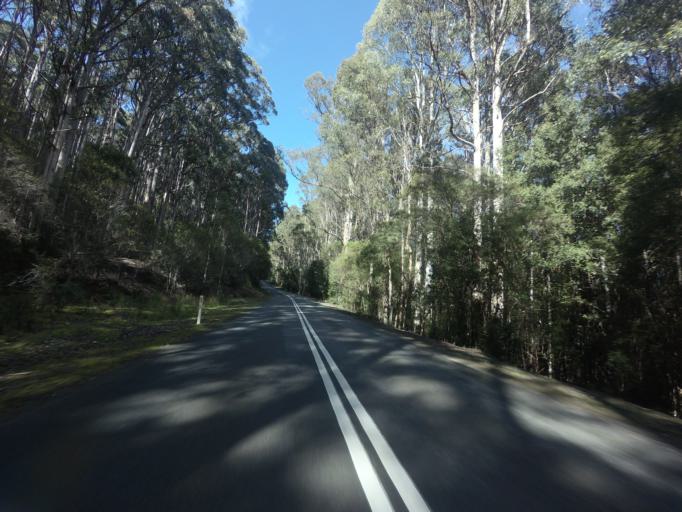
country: AU
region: Tasmania
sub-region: Derwent Valley
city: New Norfolk
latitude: -42.7336
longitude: 146.6662
